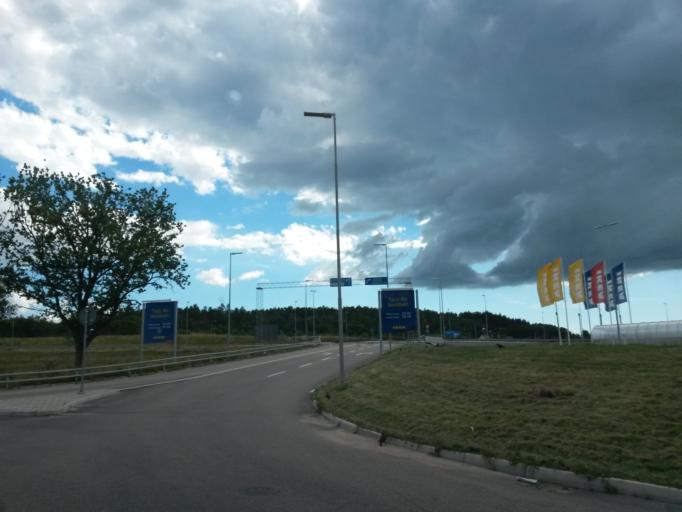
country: SE
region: Vaestra Goetaland
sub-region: Uddevalla Kommun
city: Uddevalla
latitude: 58.3545
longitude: 11.8204
